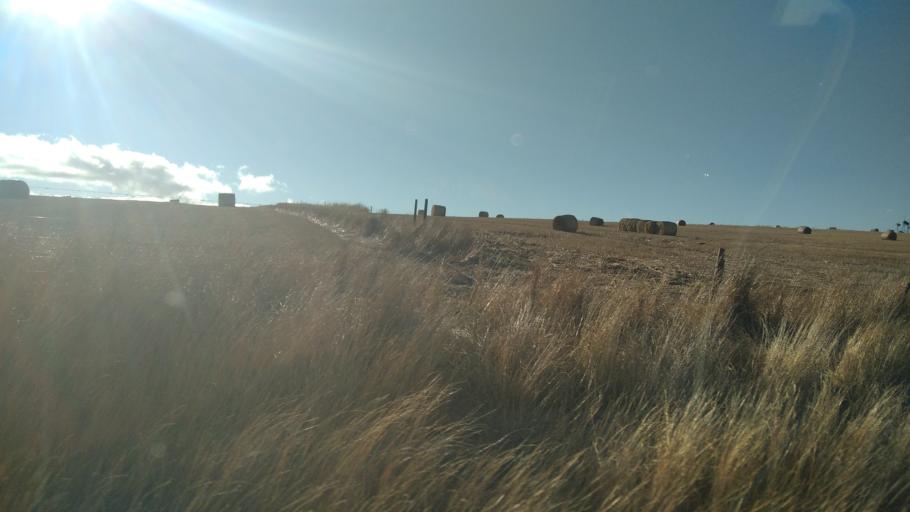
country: ZA
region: Western Cape
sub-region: Overberg District Municipality
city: Caledon
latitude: -34.1376
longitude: 19.2961
